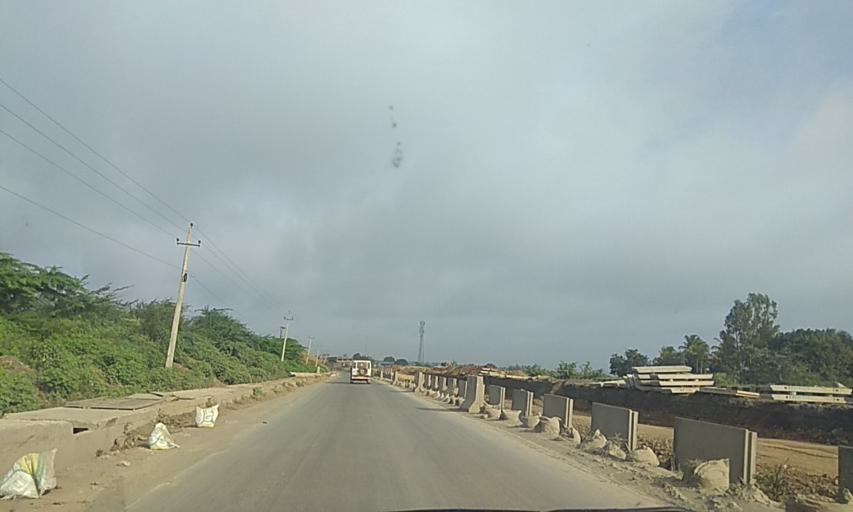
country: IN
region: Karnataka
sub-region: Haveri
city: Haveri
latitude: 14.7709
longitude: 75.4236
